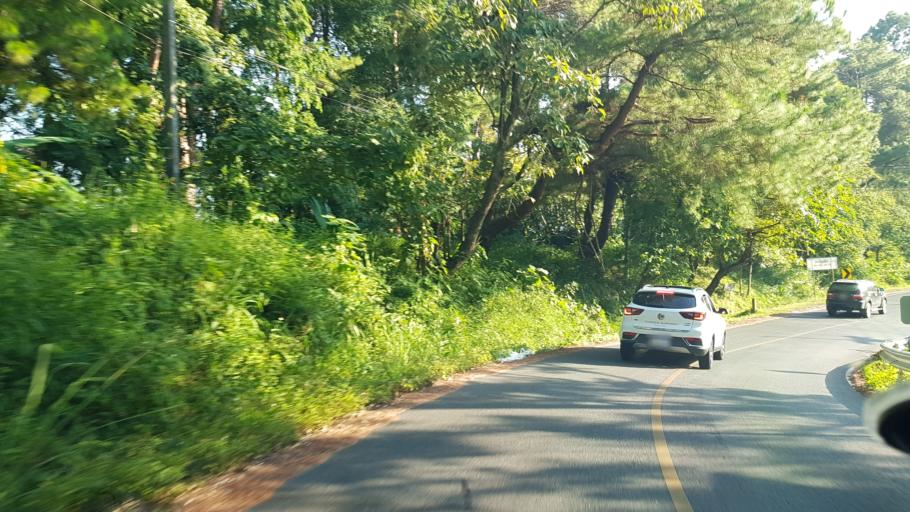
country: TH
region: Chiang Rai
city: Mae Fa Luang
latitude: 20.3127
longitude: 99.8203
